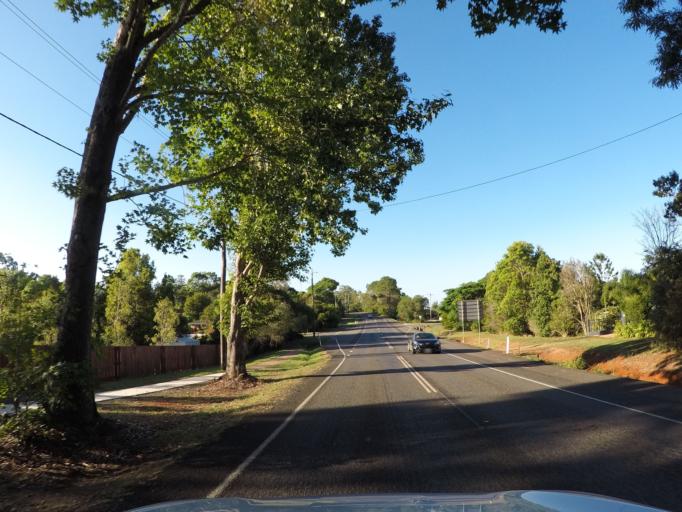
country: AU
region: Queensland
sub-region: Sunshine Coast
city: Nambour
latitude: -26.6308
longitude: 152.8676
